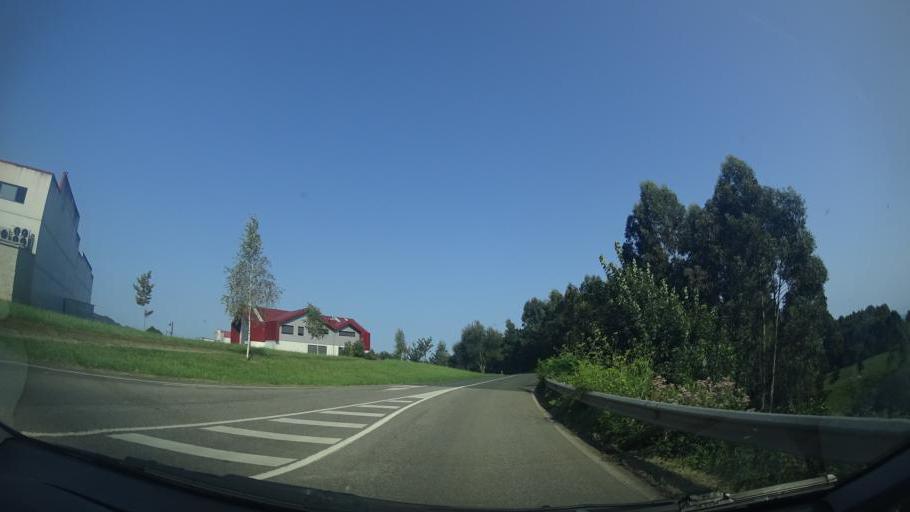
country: ES
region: Asturias
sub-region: Province of Asturias
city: Colunga
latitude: 43.4627
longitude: -5.1968
